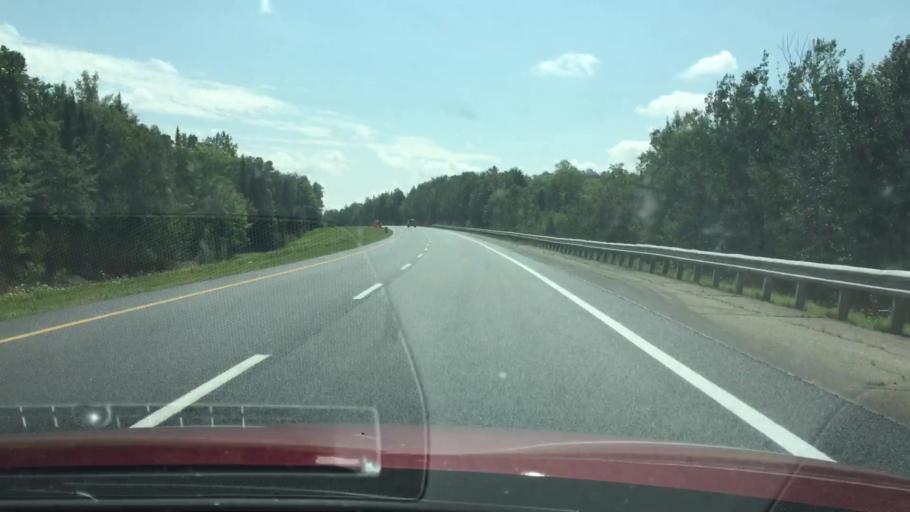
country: US
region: Maine
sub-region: Penobscot County
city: Patten
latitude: 45.8404
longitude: -68.4338
